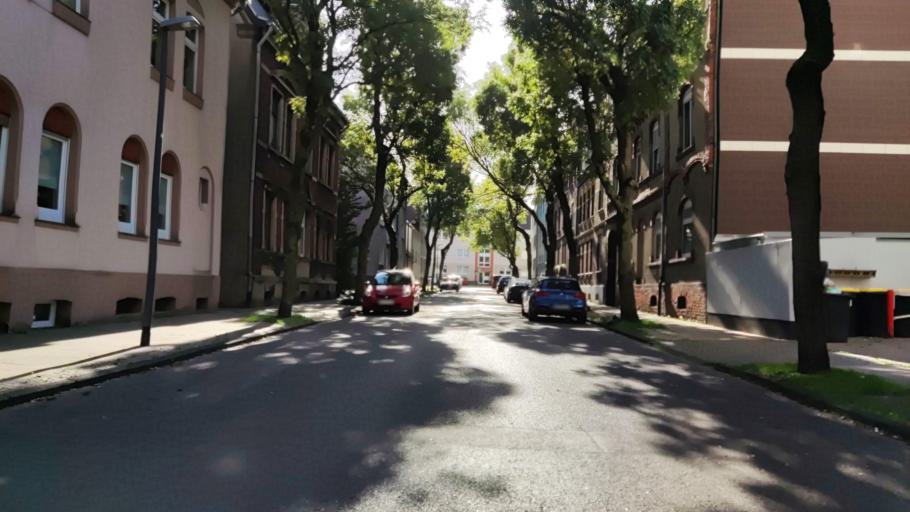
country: DE
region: North Rhine-Westphalia
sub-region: Regierungsbezirk Arnsberg
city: Herne
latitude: 51.5531
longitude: 7.2200
